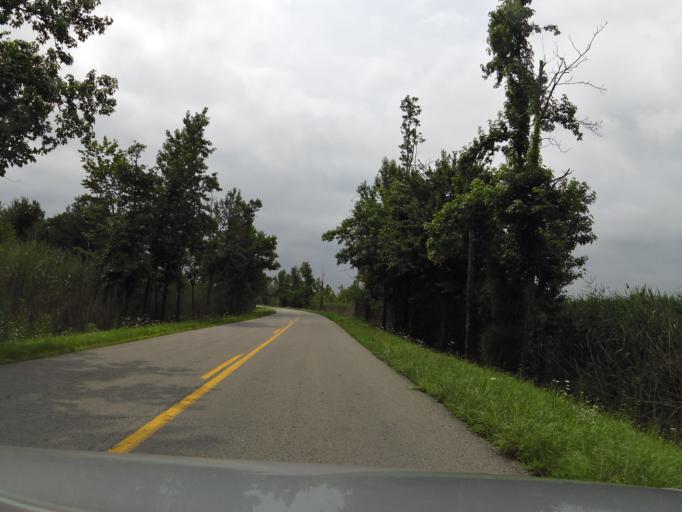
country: US
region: Kentucky
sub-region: Muhlenberg County
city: Morehead
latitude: 37.3006
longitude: -87.3205
